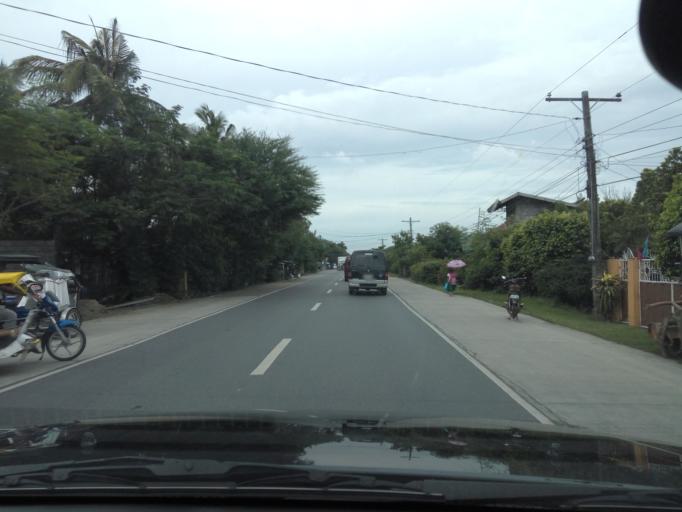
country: PH
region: Central Luzon
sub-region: Province of Nueva Ecija
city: Concepcion
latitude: 15.4477
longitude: 120.8126
